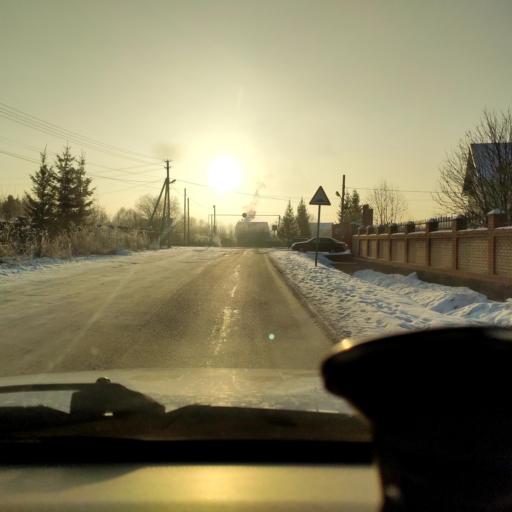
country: RU
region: Perm
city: Ferma
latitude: 57.9456
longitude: 56.3586
